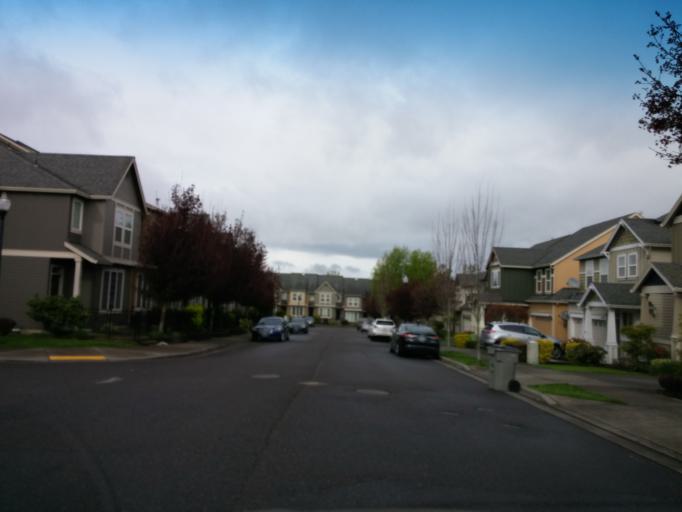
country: US
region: Oregon
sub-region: Washington County
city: Oak Hills
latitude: 45.5375
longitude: -122.8512
